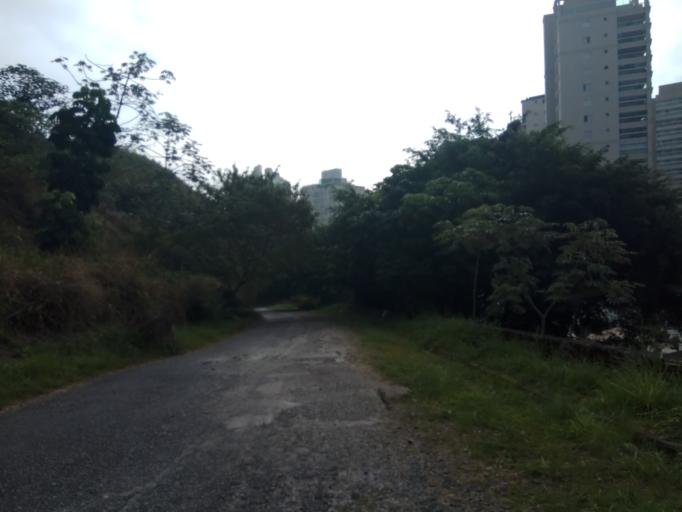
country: BR
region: Sao Paulo
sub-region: Guaruja
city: Guaruja
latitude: -24.0118
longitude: -46.2667
